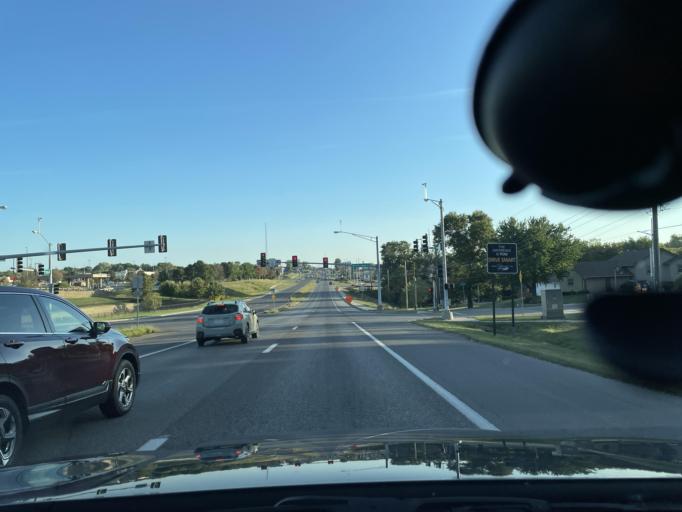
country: US
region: Missouri
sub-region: Andrew County
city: Country Club Village
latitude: 39.8115
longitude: -94.8153
